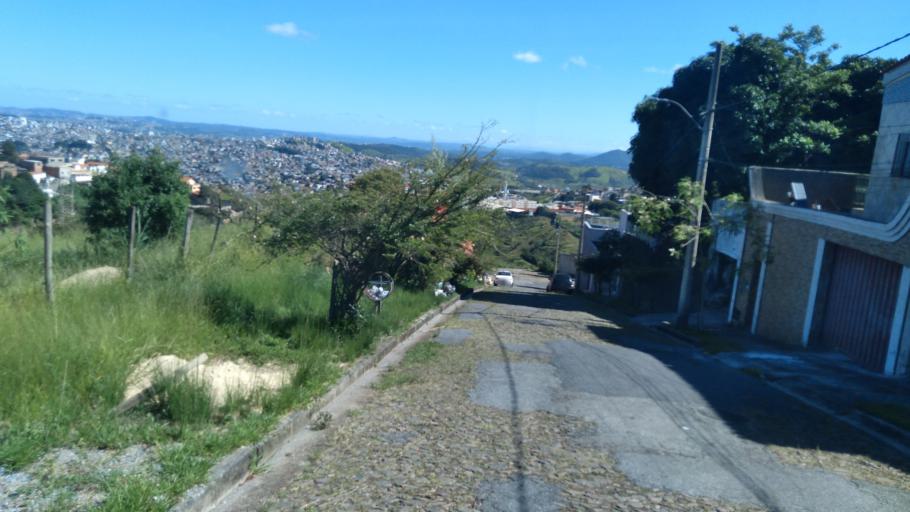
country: BR
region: Minas Gerais
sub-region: Belo Horizonte
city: Belo Horizonte
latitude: -19.9250
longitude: -43.8914
